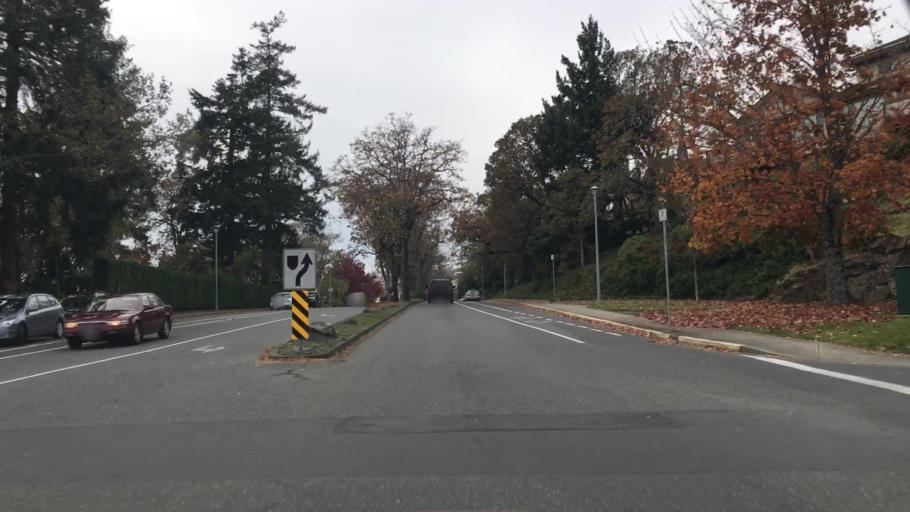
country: CA
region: British Columbia
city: Victoria
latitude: 48.4976
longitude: -123.3751
